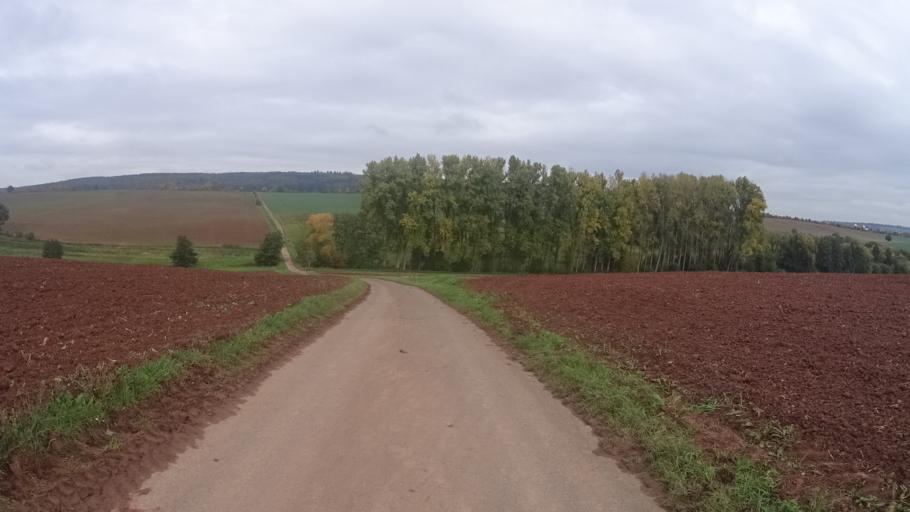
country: DE
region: Rheinland-Pfalz
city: Bolanden
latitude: 49.6420
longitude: 7.9997
